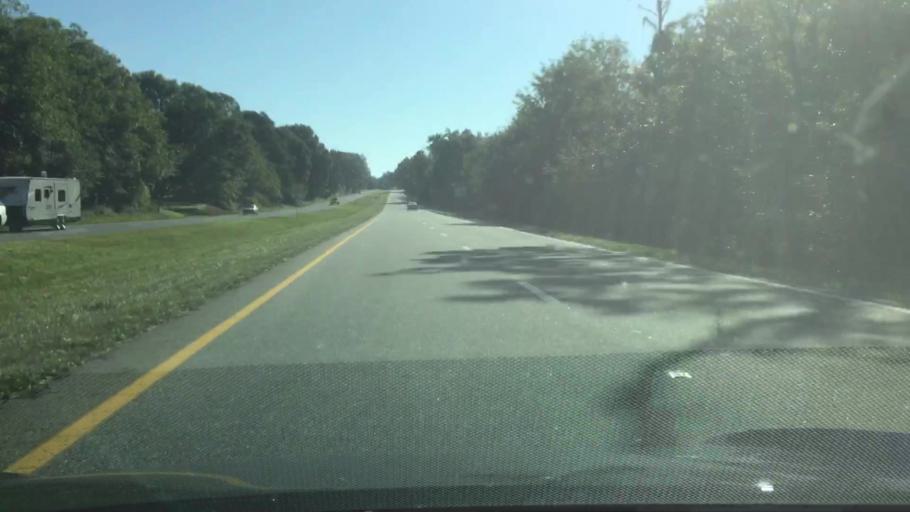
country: US
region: Virginia
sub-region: City of Bedford
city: Bedford
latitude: 37.3499
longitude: -79.6149
